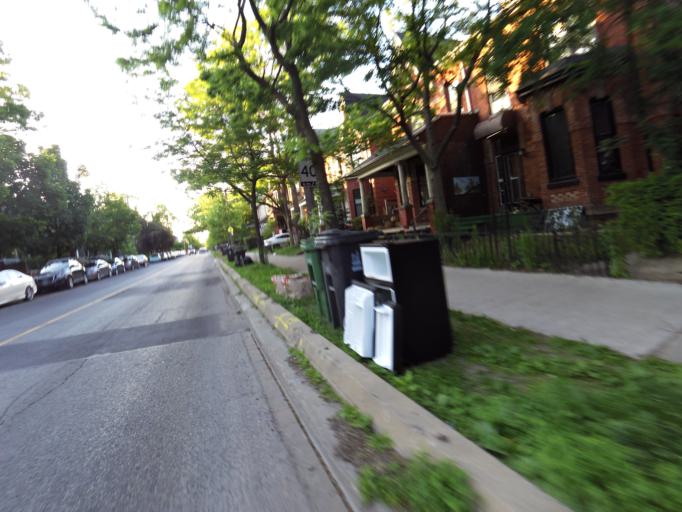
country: CA
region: Ontario
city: Toronto
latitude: 43.6411
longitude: -79.4368
